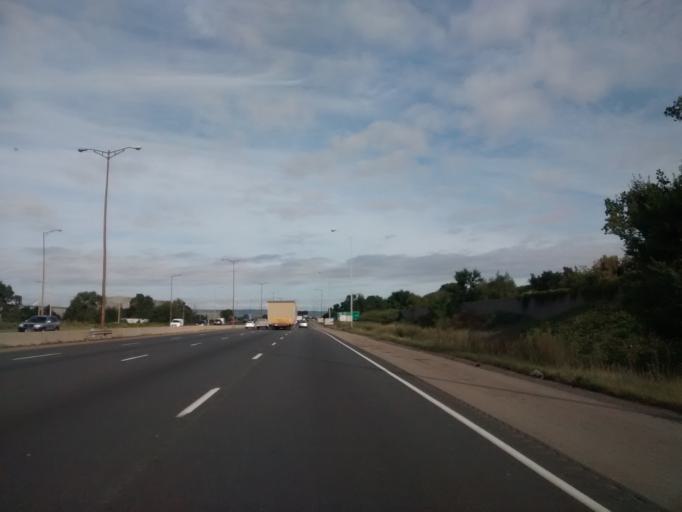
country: CA
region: Ontario
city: Hamilton
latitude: 43.2731
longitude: -79.7811
